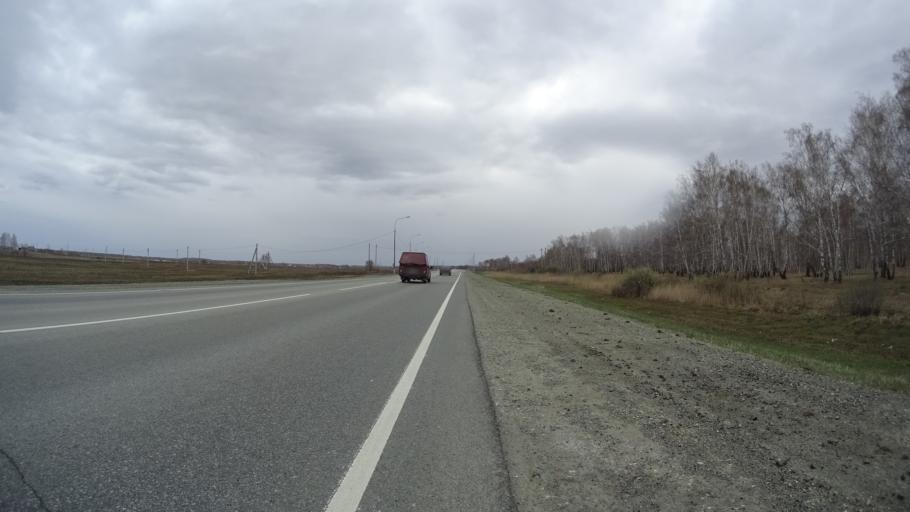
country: RU
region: Chelyabinsk
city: Krasnogorskiy
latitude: 54.6866
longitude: 61.2478
